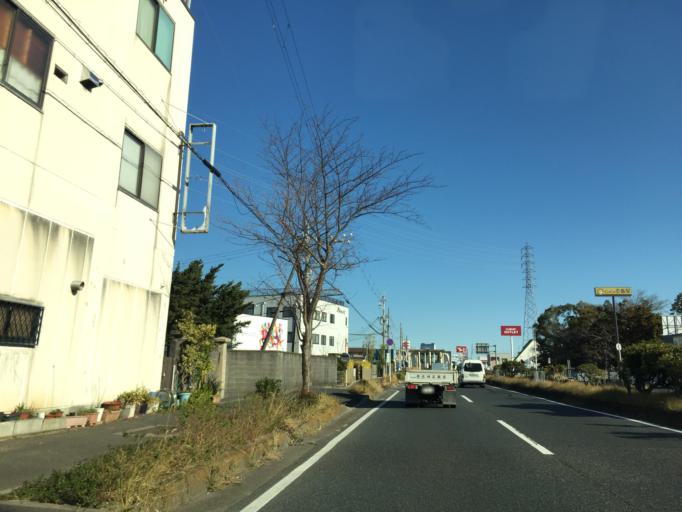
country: JP
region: Osaka
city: Kaizuka
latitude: 34.3929
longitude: 135.3055
